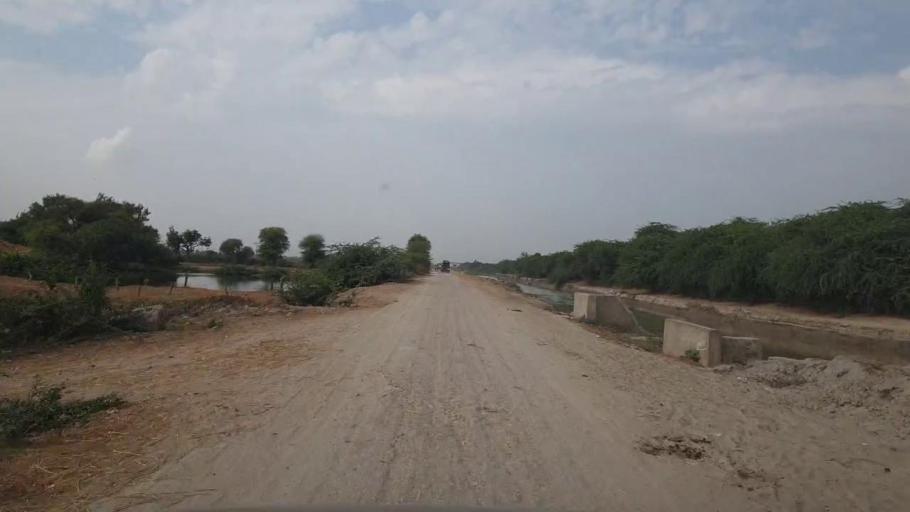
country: PK
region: Sindh
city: Kario
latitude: 24.6345
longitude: 68.5679
